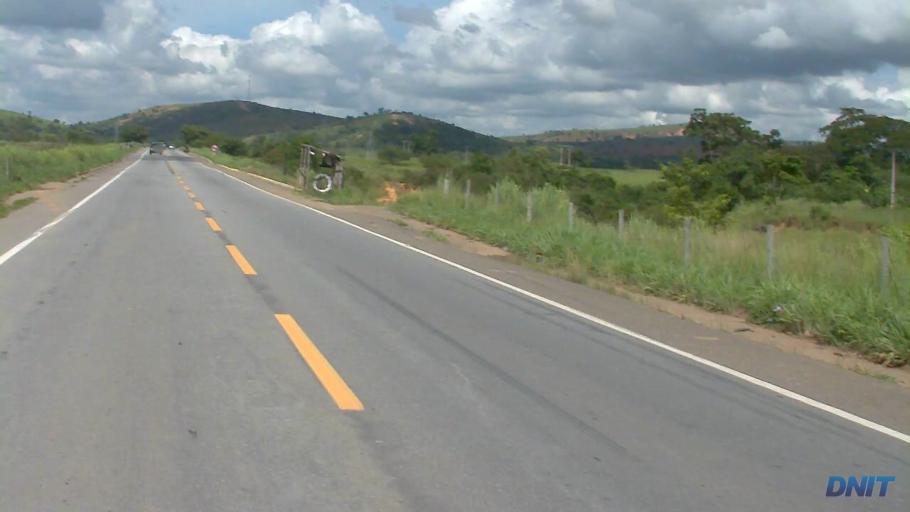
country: BR
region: Minas Gerais
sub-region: Governador Valadares
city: Governador Valadares
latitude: -19.0088
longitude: -42.1353
